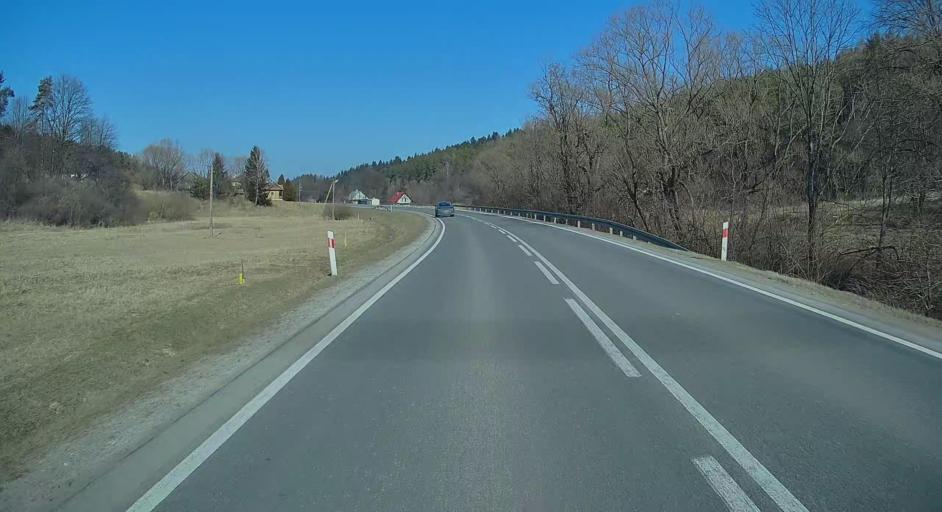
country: PL
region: Subcarpathian Voivodeship
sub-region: Powiat przemyski
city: Bircza
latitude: 49.6776
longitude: 22.4351
